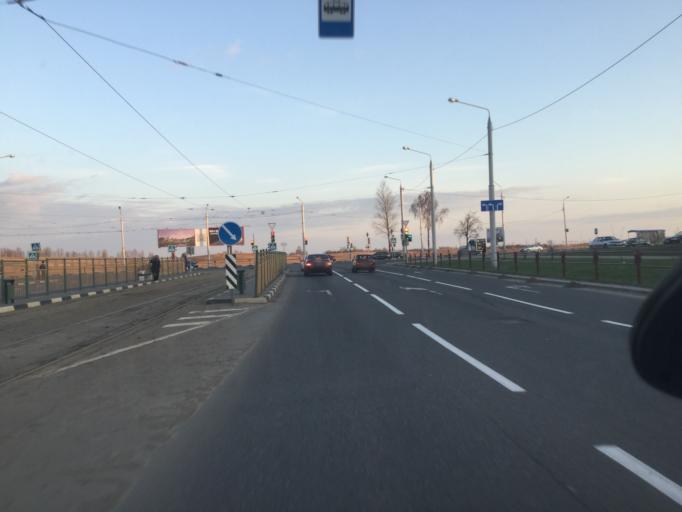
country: BY
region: Vitebsk
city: Vitebsk
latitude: 55.1605
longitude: 30.1694
